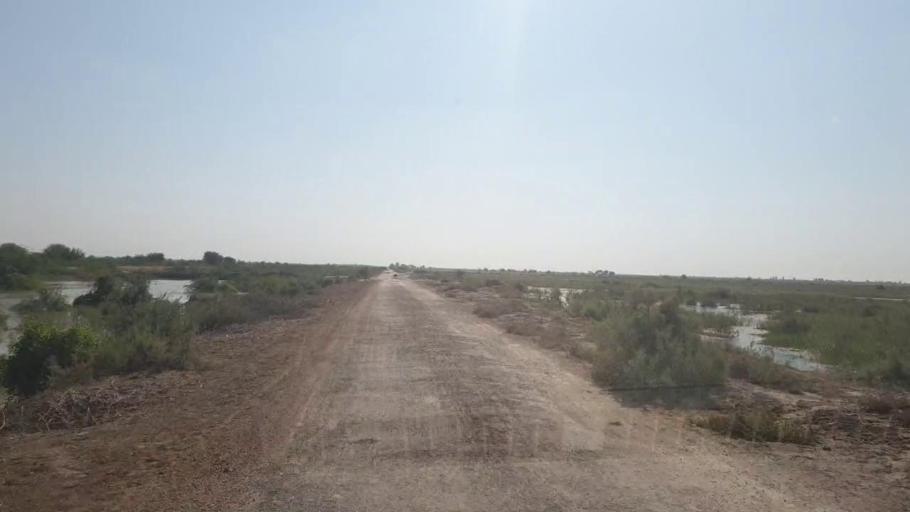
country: PK
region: Sindh
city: Tando Bago
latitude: 24.8640
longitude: 69.1643
